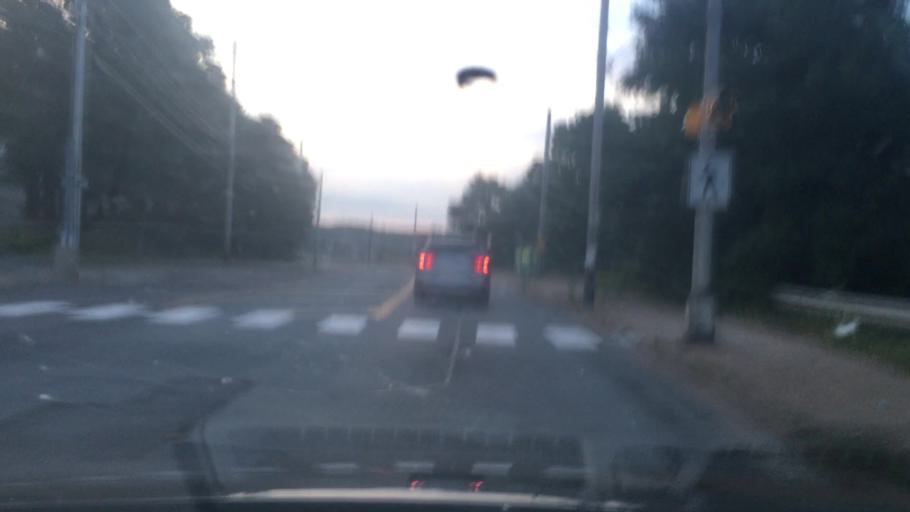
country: CA
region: Nova Scotia
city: Dartmouth
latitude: 44.6786
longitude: -63.6503
